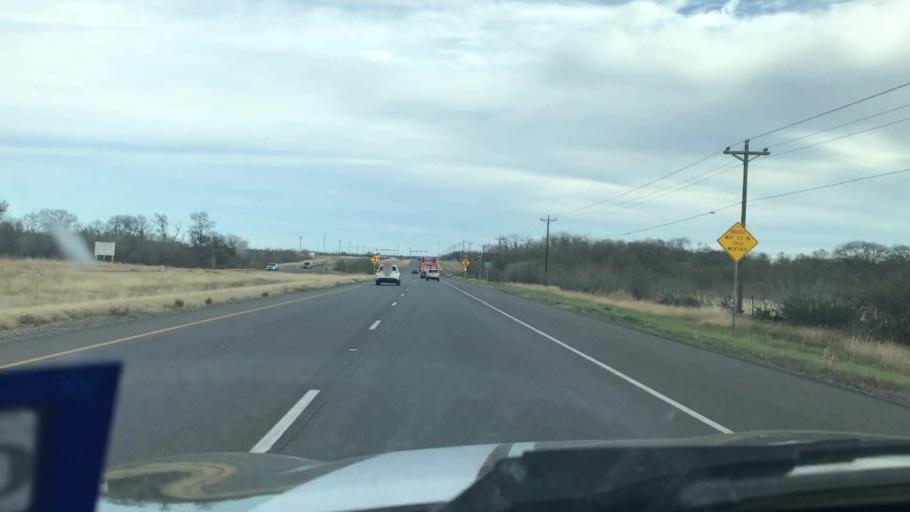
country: US
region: Texas
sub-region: Bastrop County
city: Elgin
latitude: 30.3515
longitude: -97.4401
